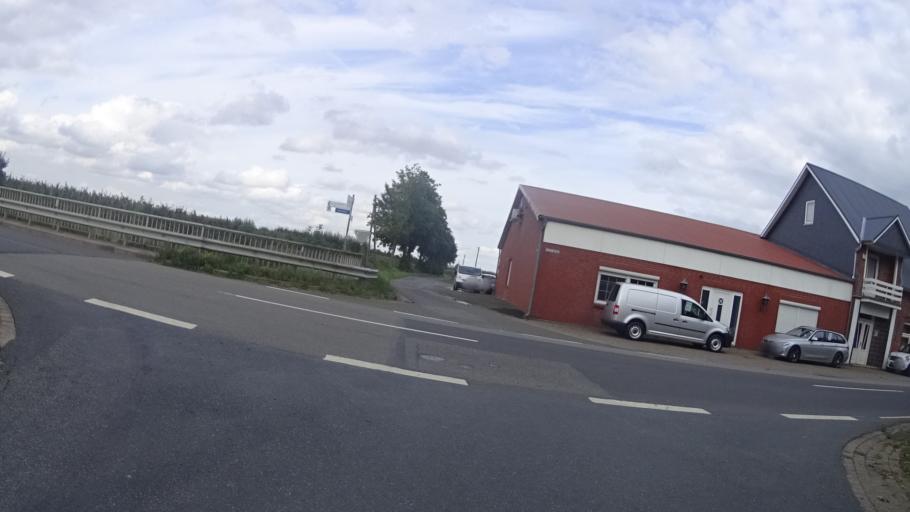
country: DE
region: Lower Saxony
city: Grossenworden
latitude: 53.7022
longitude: 9.2545
